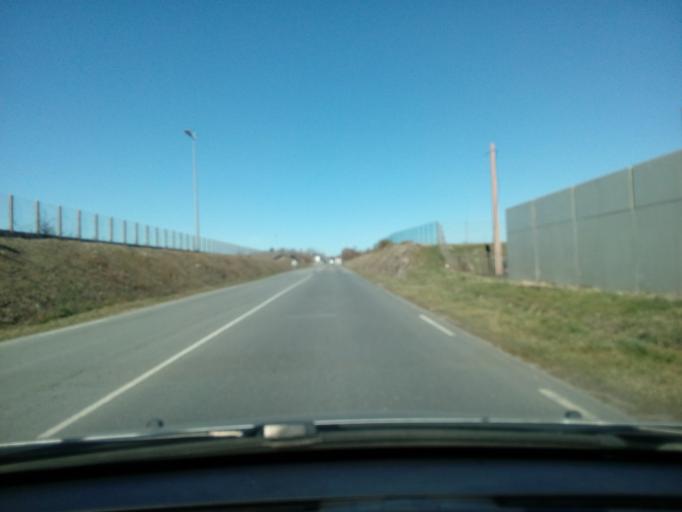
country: FR
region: Limousin
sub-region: Departement de la Creuse
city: Gueret
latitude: 46.1880
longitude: 1.8770
